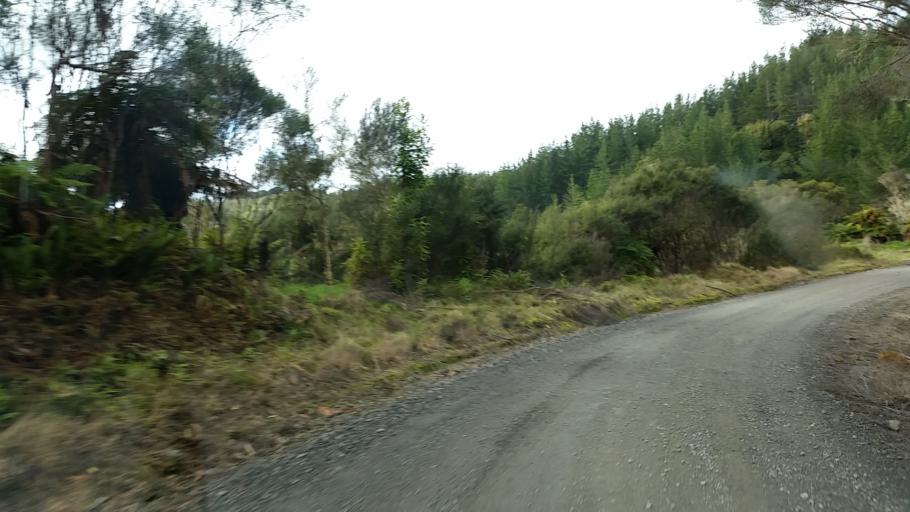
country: NZ
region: Taranaki
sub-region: New Plymouth District
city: Waitara
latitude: -39.1570
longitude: 174.5548
